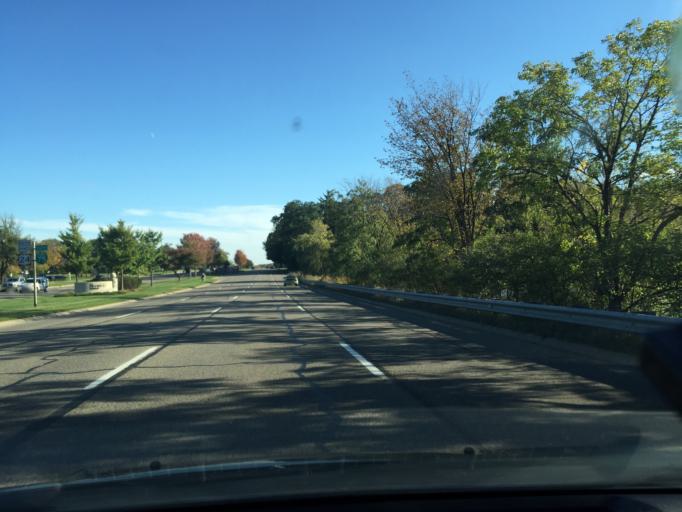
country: US
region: Michigan
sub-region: Oakland County
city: Pontiac
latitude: 42.6117
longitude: -83.2721
